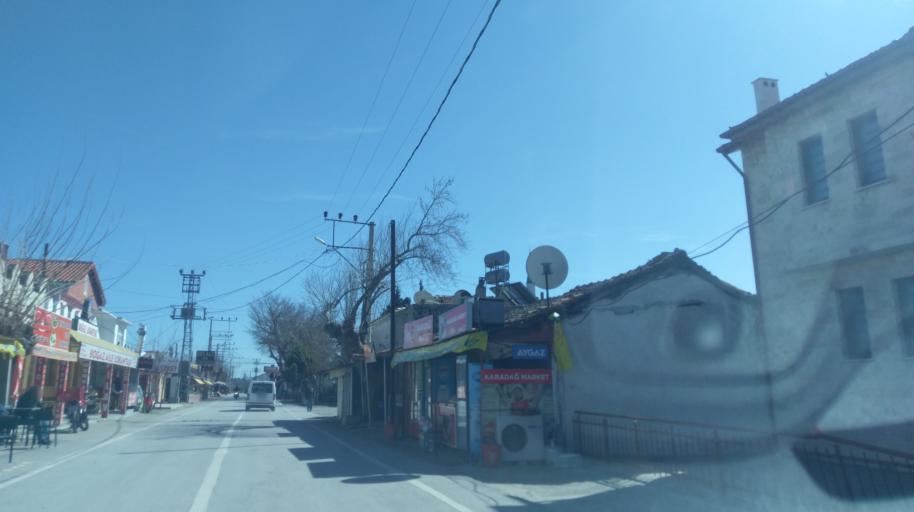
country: TR
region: Canakkale
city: Intepe
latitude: 40.0943
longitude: 26.2247
